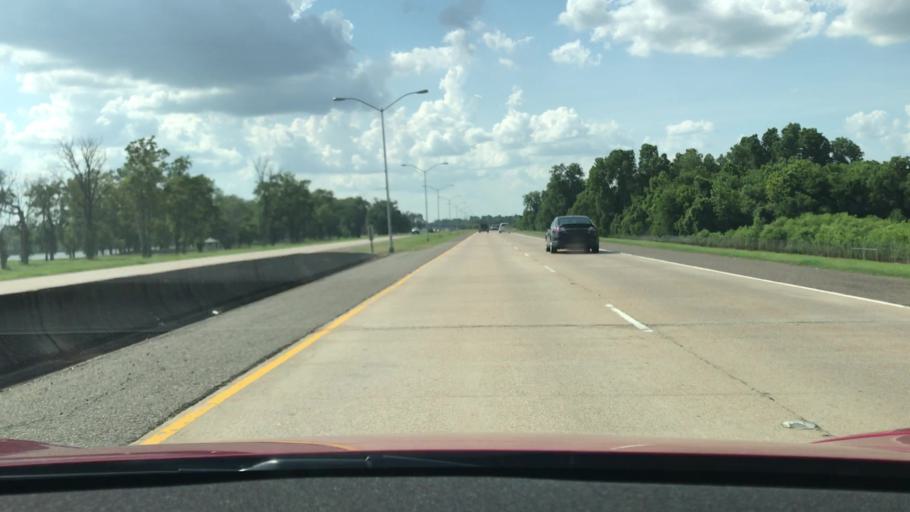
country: US
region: Louisiana
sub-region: Bossier Parish
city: Bossier City
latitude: 32.4847
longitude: -93.6864
